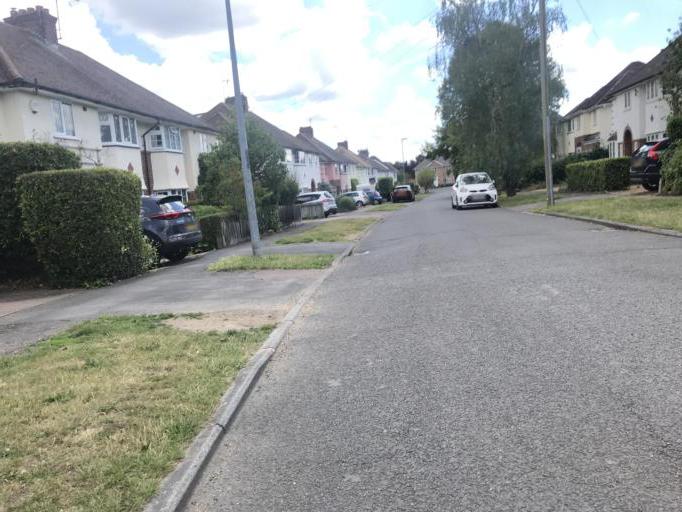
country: GB
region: England
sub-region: Cambridgeshire
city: Girton
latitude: 52.2273
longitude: 0.0896
